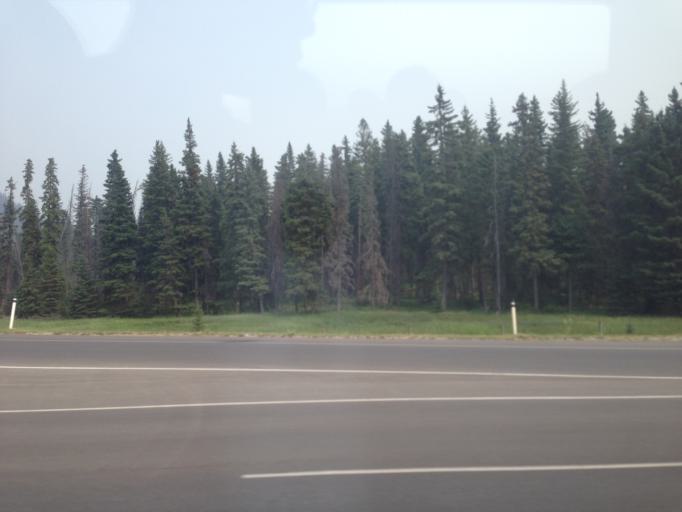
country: CA
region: Alberta
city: Banff
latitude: 51.1870
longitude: -115.5827
